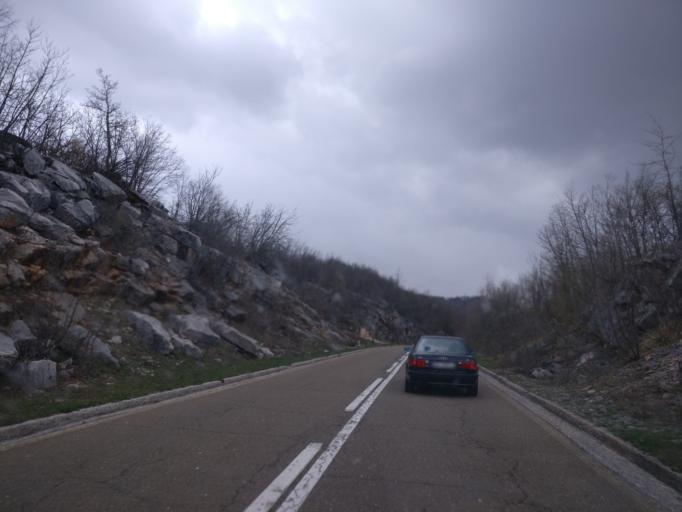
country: ME
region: Opstina Niksic
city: Niksic
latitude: 42.9226
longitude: 18.9457
